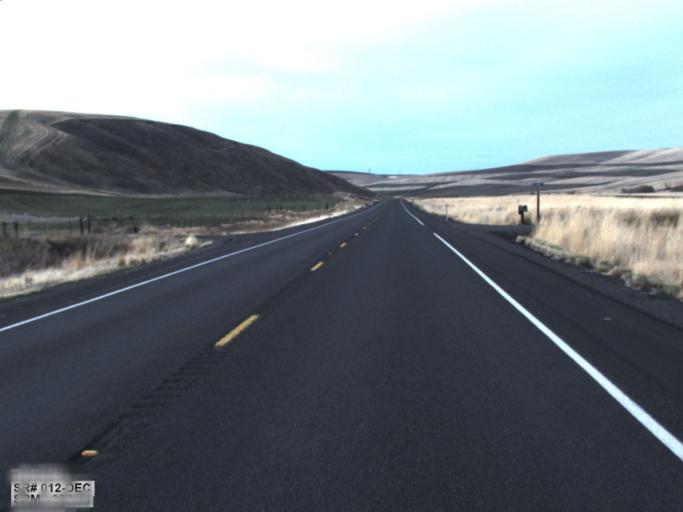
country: US
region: Washington
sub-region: Columbia County
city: Dayton
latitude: 46.5365
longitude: -117.8550
